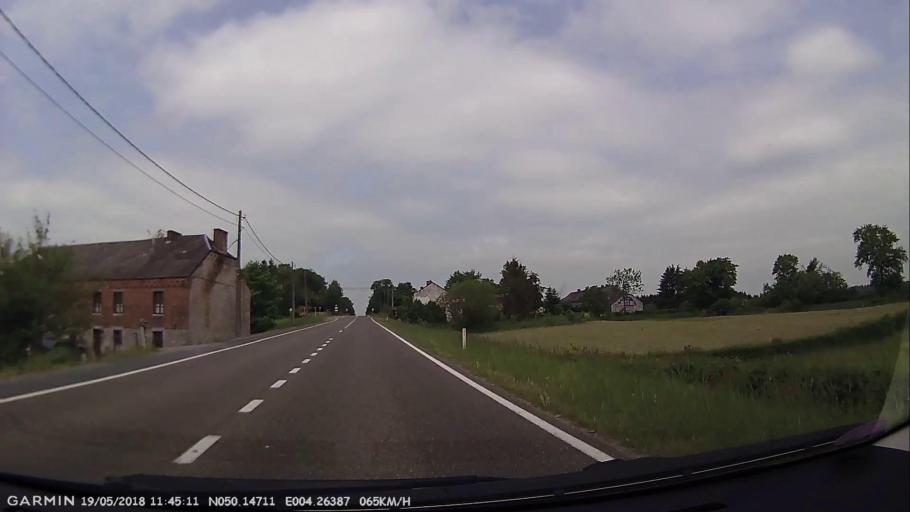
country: BE
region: Wallonia
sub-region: Province du Hainaut
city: Froidchapelle
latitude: 50.1473
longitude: 4.2637
